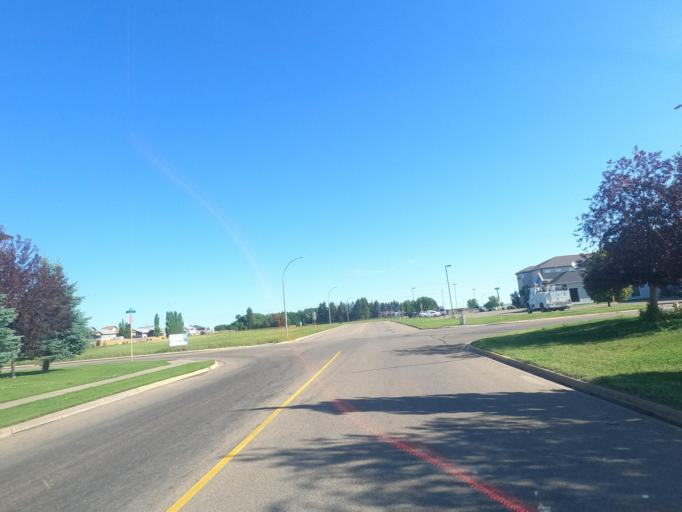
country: CA
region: Alberta
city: Brooks
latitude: 50.5838
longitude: -111.9000
